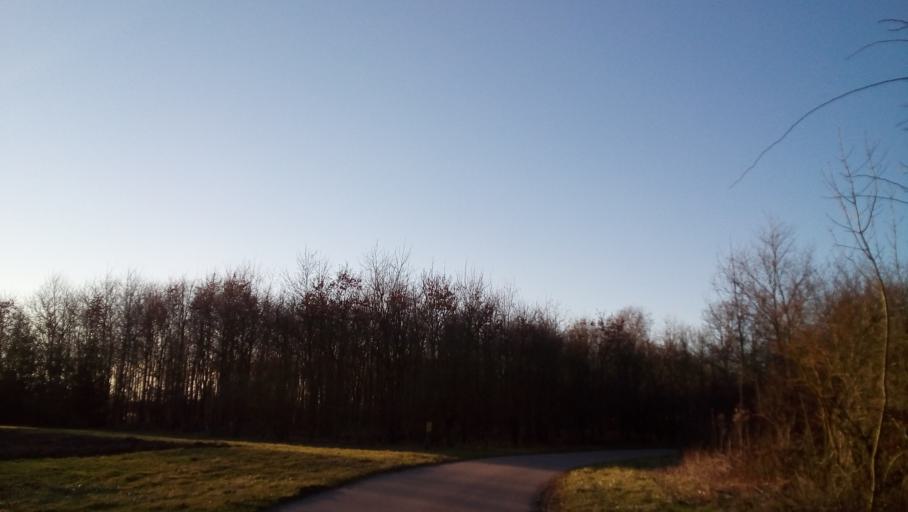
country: DE
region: Baden-Wuerttemberg
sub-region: Karlsruhe Region
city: Lichtenau
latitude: 48.6879
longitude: 7.9923
